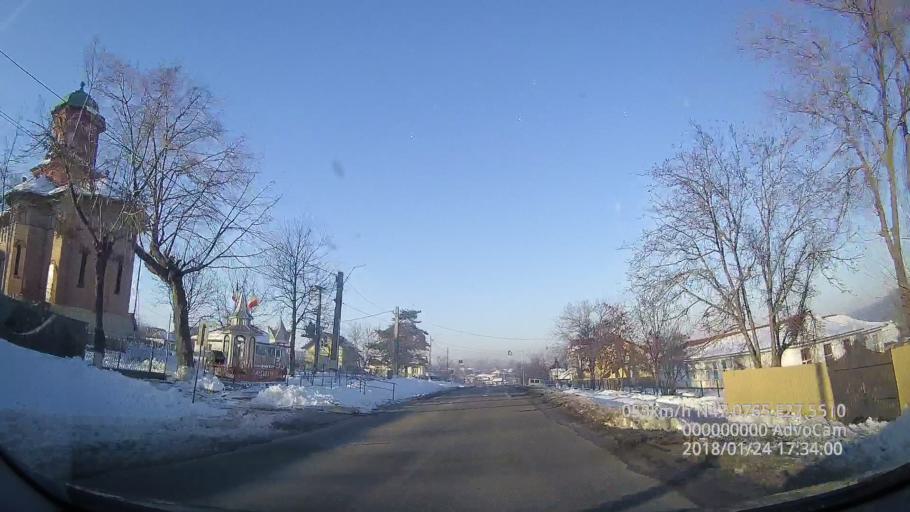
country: RO
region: Iasi
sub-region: Comuna Ciurea
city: Dumbrava
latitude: 47.0769
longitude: 27.5509
